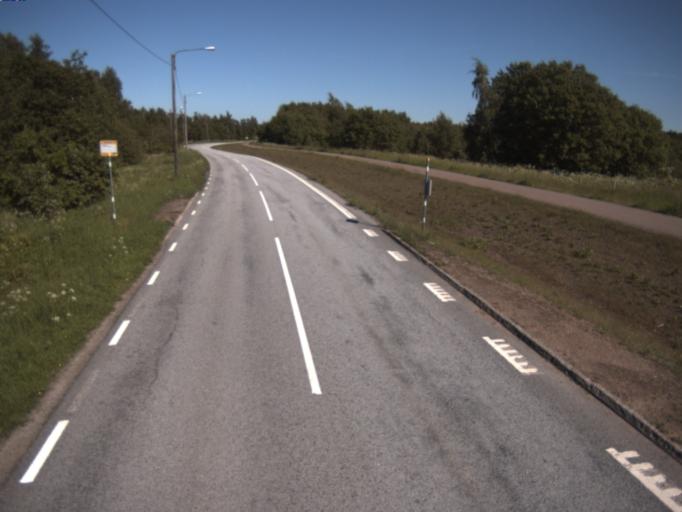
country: SE
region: Skane
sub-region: Helsingborg
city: Gantofta
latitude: 55.9931
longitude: 12.7920
